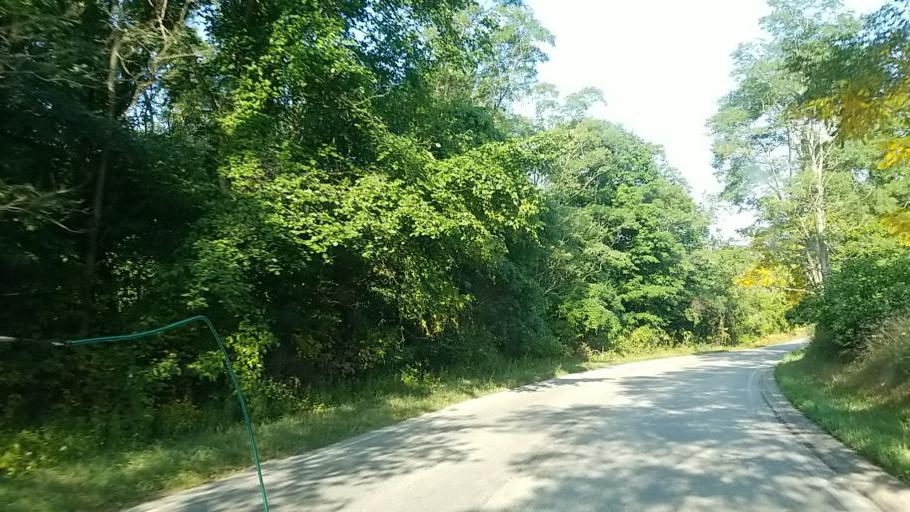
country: US
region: Michigan
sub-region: Newaygo County
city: Fremont
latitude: 43.3461
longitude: -85.9316
